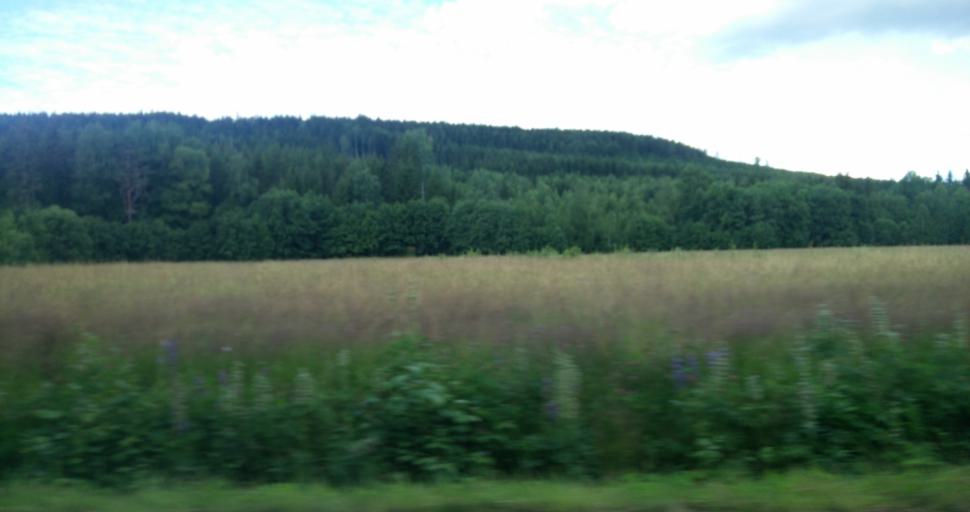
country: SE
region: Vaermland
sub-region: Hagfors Kommun
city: Ekshaerad
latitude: 60.0602
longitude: 13.4793
